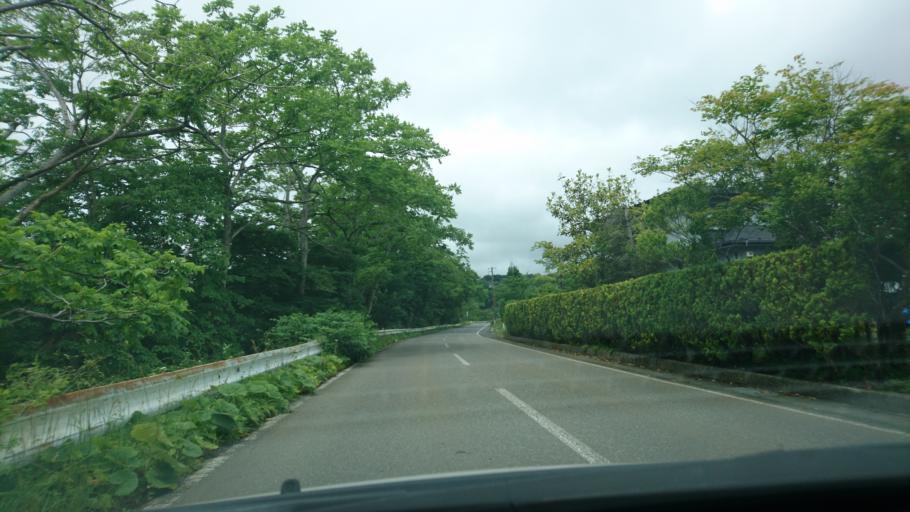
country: JP
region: Iwate
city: Ichinoseki
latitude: 38.9459
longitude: 141.0425
